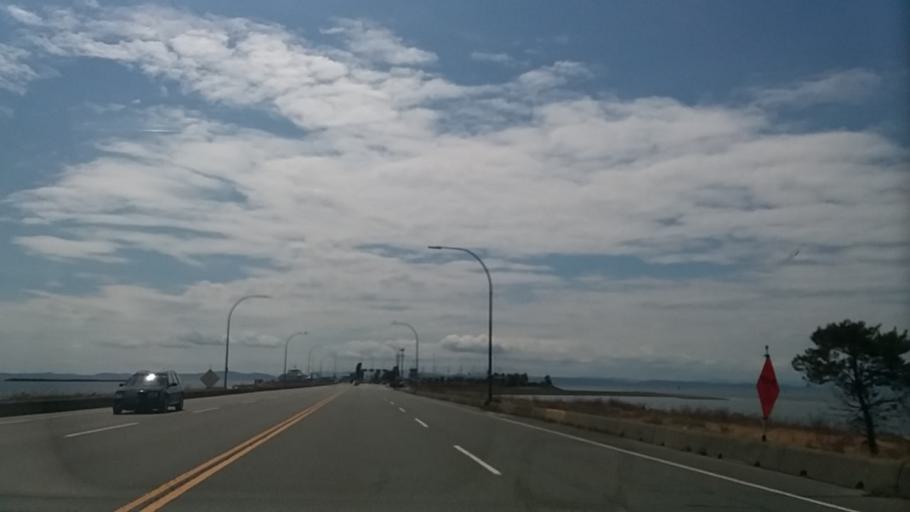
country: US
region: Washington
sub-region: Whatcom County
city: Point Roberts
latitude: 49.0156
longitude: -123.1172
